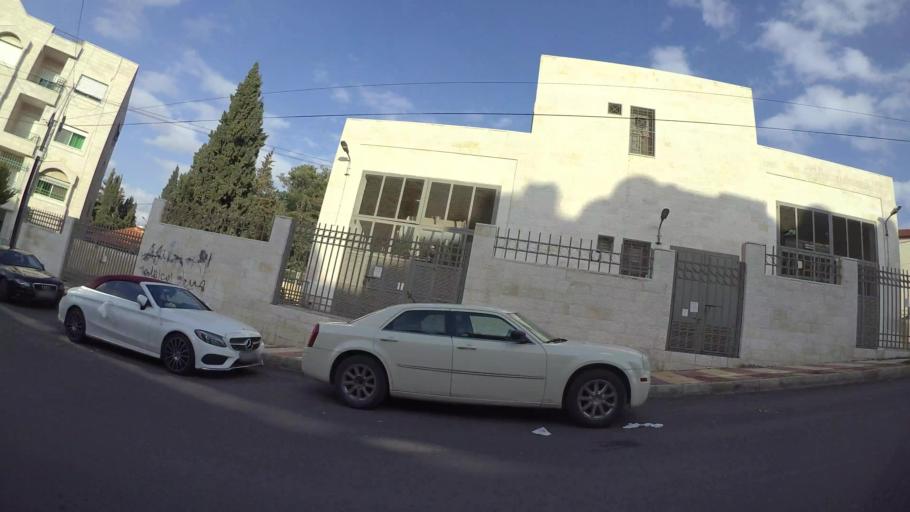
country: JO
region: Amman
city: Al Jubayhah
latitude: 31.9849
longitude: 35.8756
